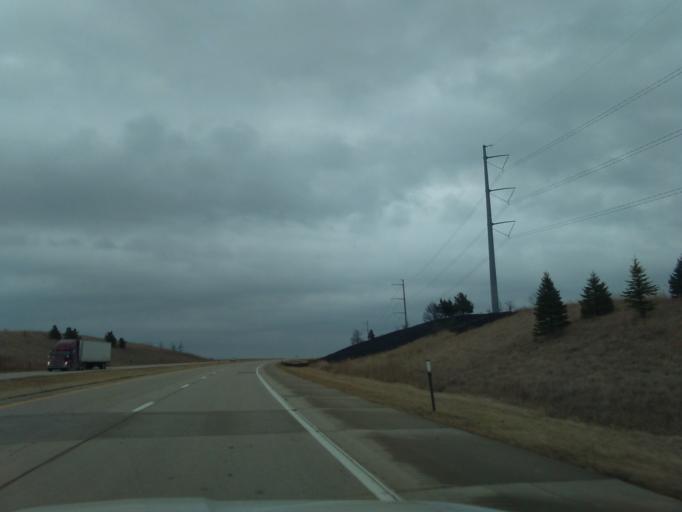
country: US
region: Nebraska
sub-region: Otoe County
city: Syracuse
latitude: 40.6752
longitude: -96.0772
